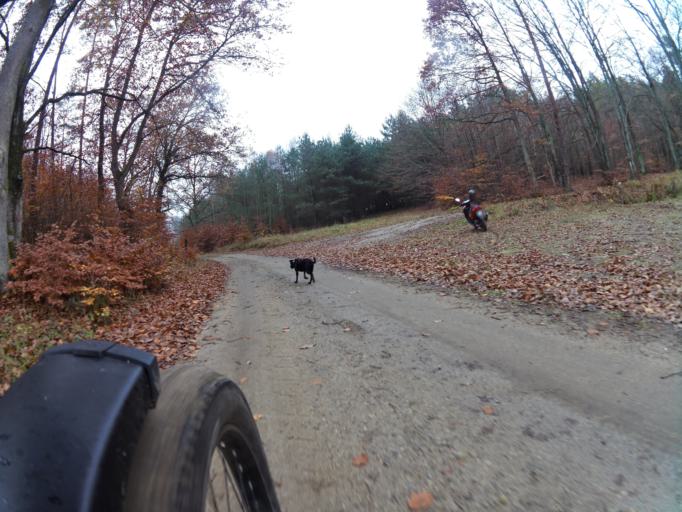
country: PL
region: Pomeranian Voivodeship
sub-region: Powiat pucki
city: Krokowa
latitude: 54.7144
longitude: 18.1410
